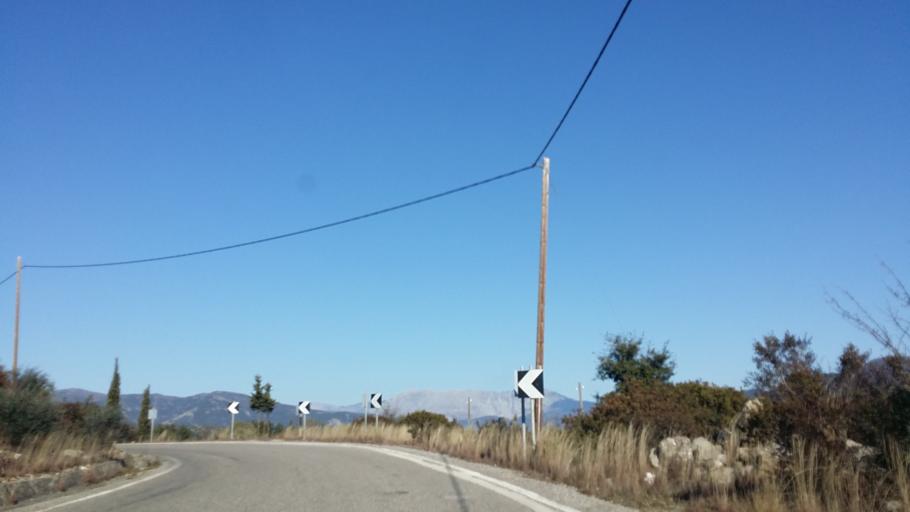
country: GR
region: West Greece
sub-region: Nomos Aitolias kai Akarnanias
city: Lepenou
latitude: 38.8179
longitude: 21.3348
